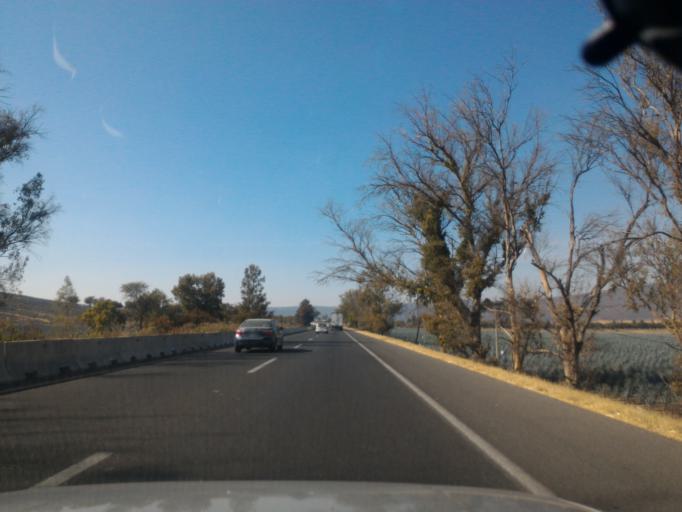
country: MX
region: Jalisco
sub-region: Poncitlan
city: Cuitzeo (La Estancia)
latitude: 20.3600
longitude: -102.8030
